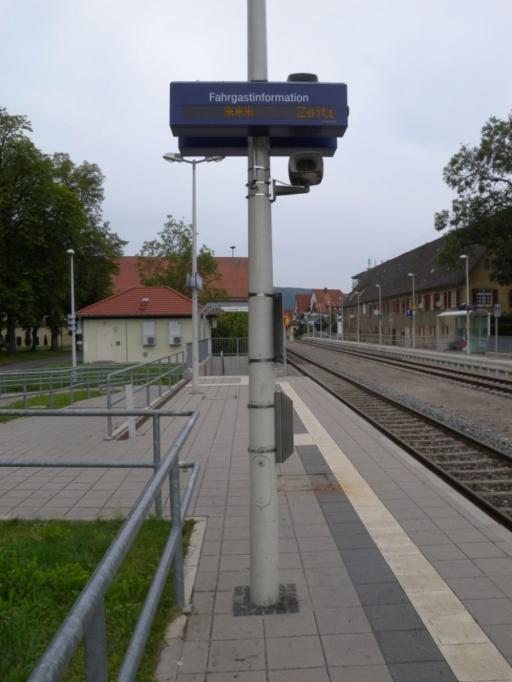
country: DE
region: Baden-Wuerttemberg
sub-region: Regierungsbezirk Stuttgart
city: Konigsbronn
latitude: 48.7392
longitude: 10.1166
